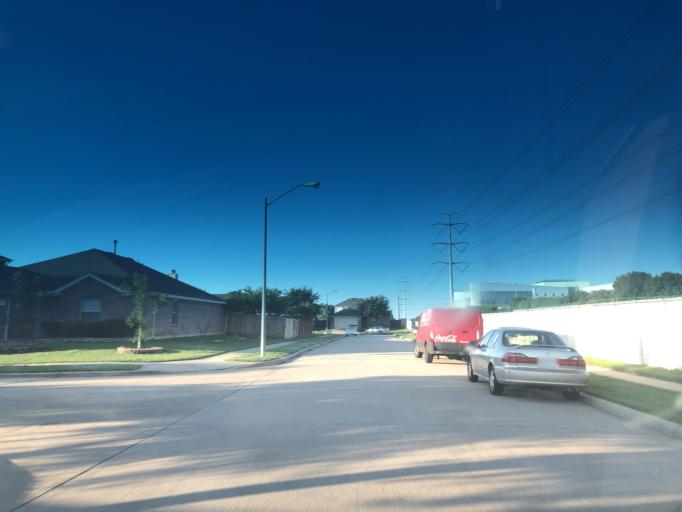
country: US
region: Texas
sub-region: Dallas County
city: Grand Prairie
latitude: 32.7035
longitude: -97.0222
